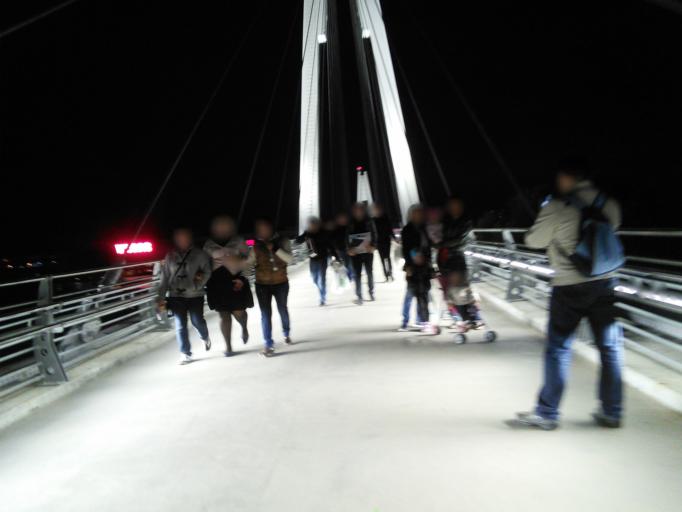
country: RU
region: Moskovskaya
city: Pavshino
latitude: 55.8211
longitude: 37.3796
